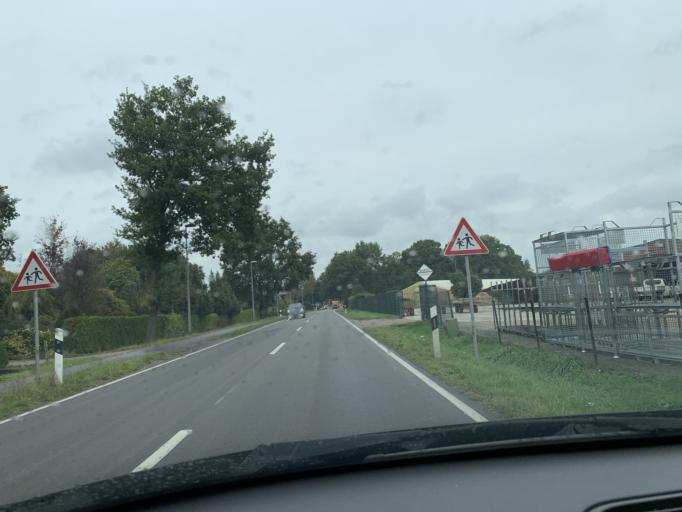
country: DE
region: Lower Saxony
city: Bad Zwischenahn
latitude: 53.1684
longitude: 8.0668
